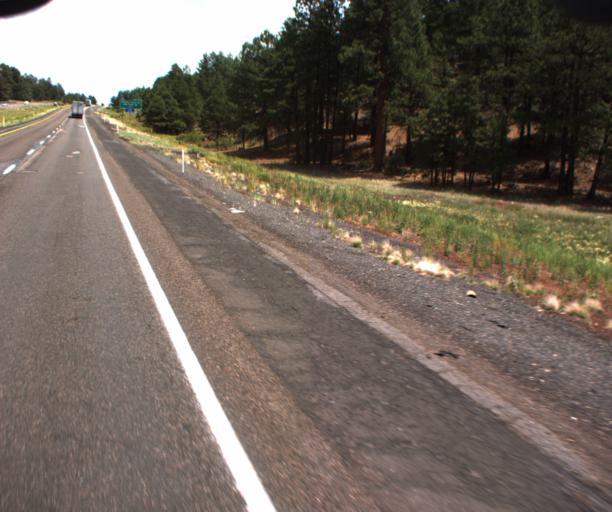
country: US
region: Arizona
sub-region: Coconino County
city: Williams
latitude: 35.2606
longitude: -112.0730
